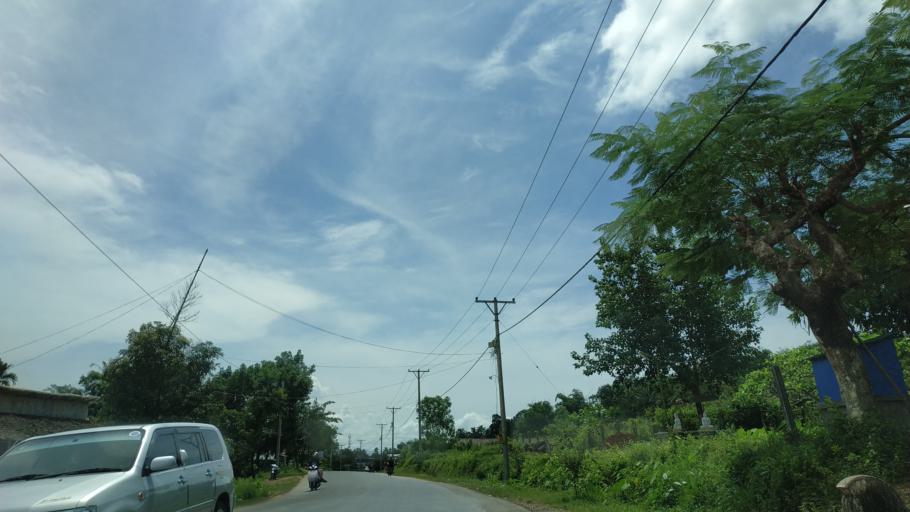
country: MM
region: Tanintharyi
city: Dawei
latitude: 14.1099
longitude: 98.1649
